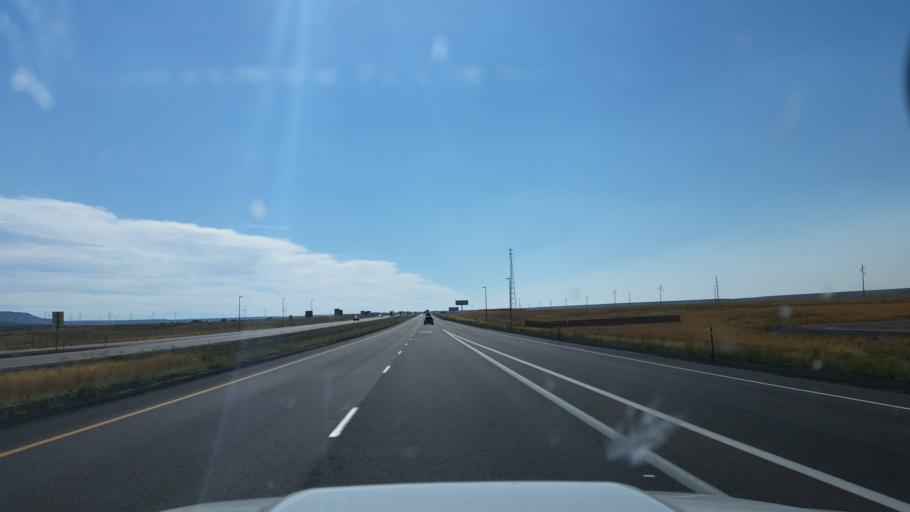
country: US
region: Wyoming
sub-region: Uinta County
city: Mountain View
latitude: 41.3310
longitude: -110.4339
